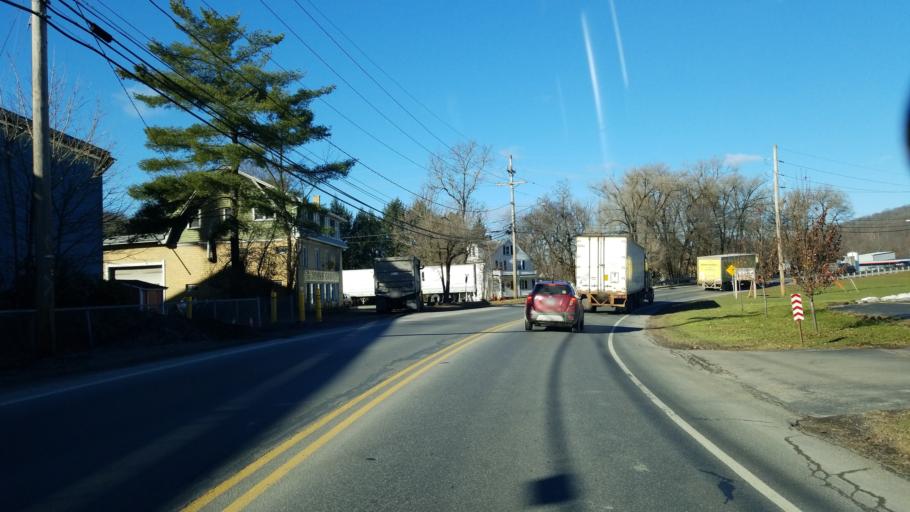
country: US
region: Pennsylvania
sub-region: Jefferson County
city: Brockway
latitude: 41.2435
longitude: -78.7872
